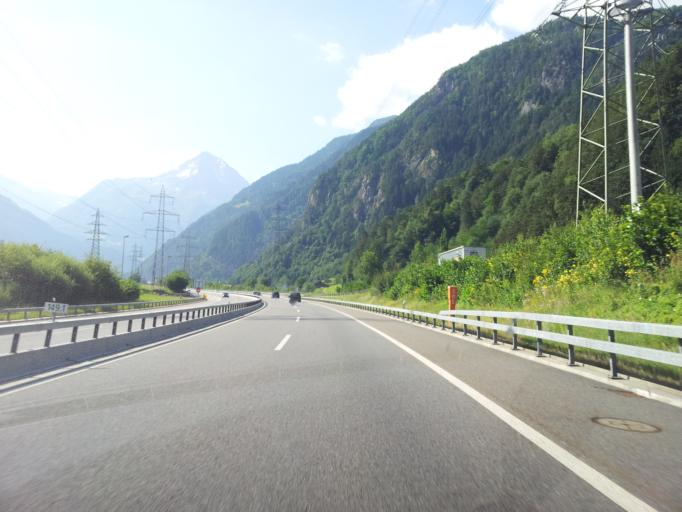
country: CH
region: Uri
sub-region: Uri
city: Erstfeld
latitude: 46.8345
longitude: 8.6367
